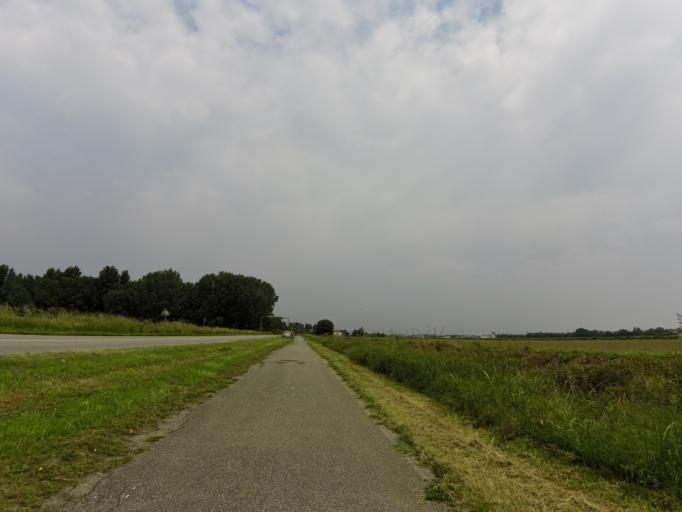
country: IT
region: Lombardy
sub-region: Citta metropolitana di Milano
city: Linate
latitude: 45.4385
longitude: 9.2738
